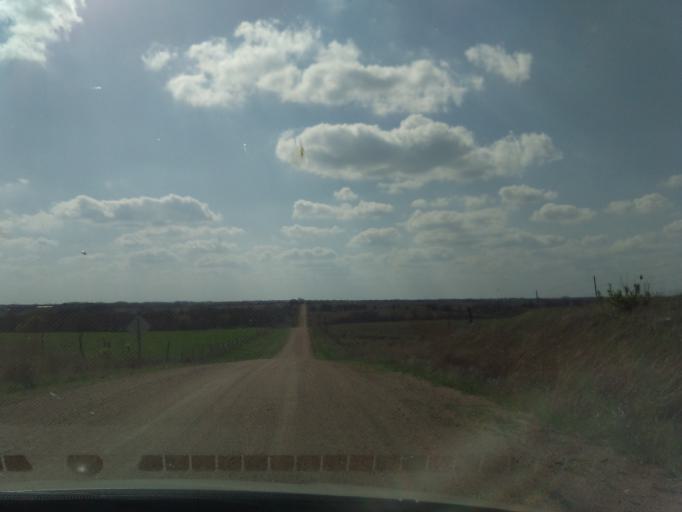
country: US
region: Nebraska
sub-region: Webster County
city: Red Cloud
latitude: 40.0025
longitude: -98.3311
